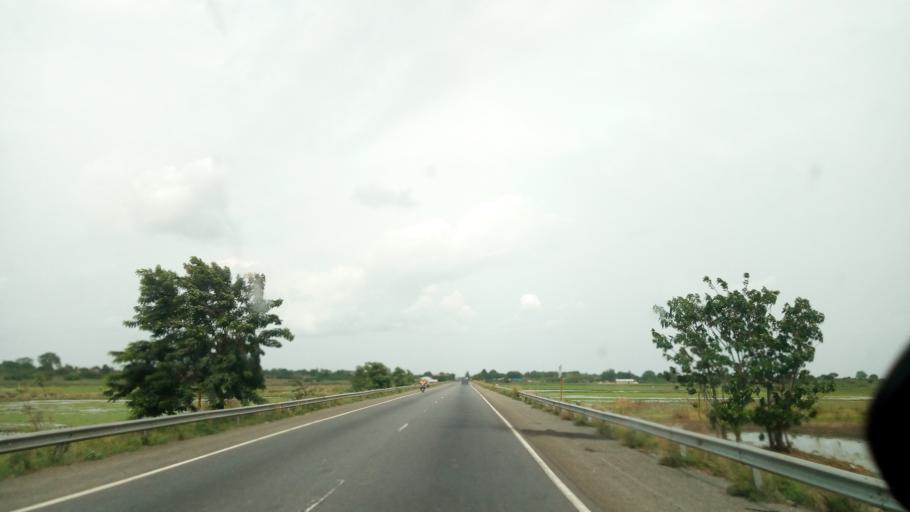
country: GH
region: Volta
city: Keta
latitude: 6.0614
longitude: 0.9352
